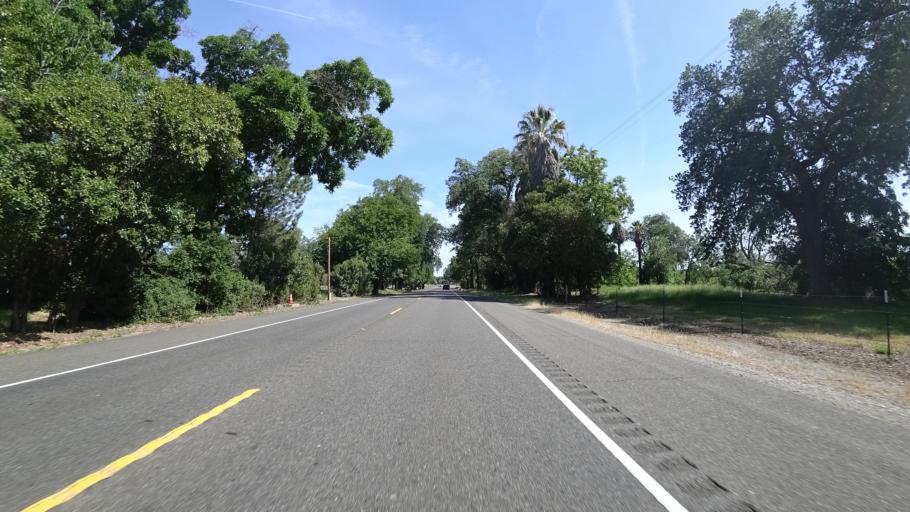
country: US
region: California
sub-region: Tehama County
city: Red Bluff
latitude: 40.1719
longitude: -122.1645
